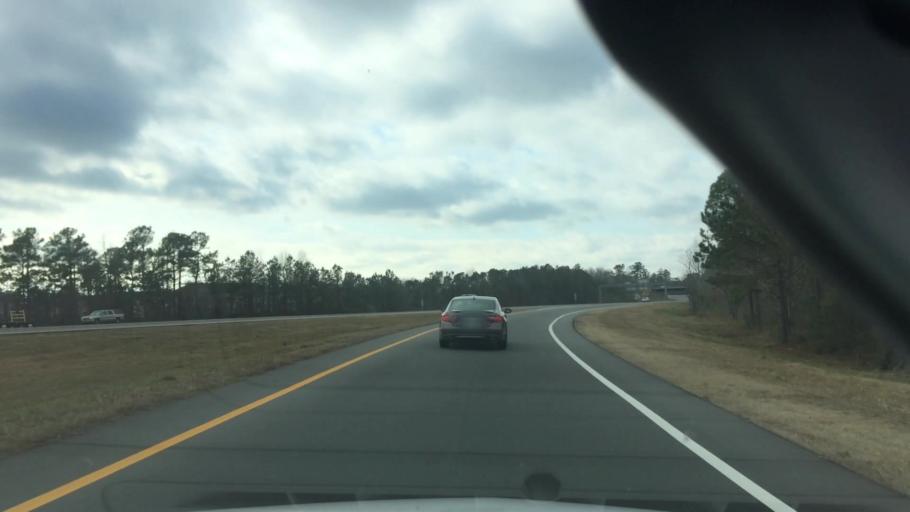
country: US
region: North Carolina
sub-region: New Hanover County
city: Murraysville
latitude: 34.3191
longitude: -77.8756
